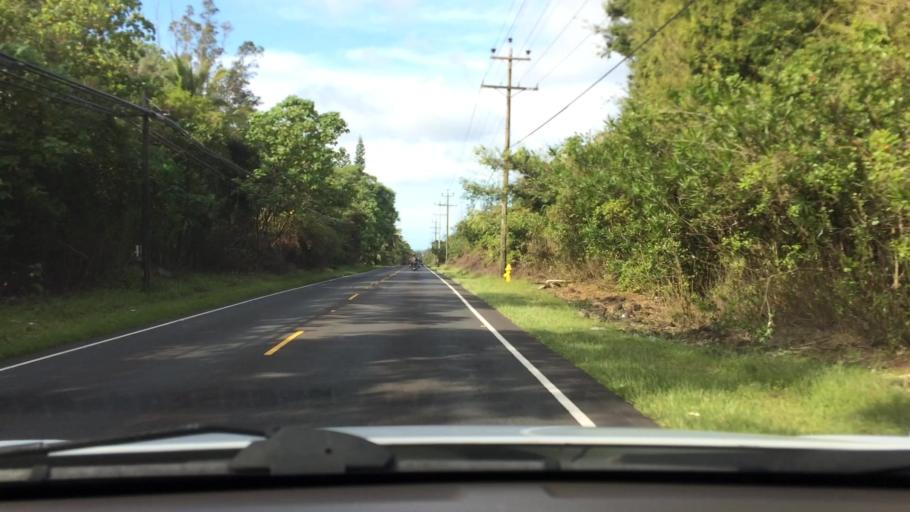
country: US
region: Hawaii
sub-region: Hawaii County
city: Hawaiian Paradise Park
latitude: 19.5100
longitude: -154.9454
